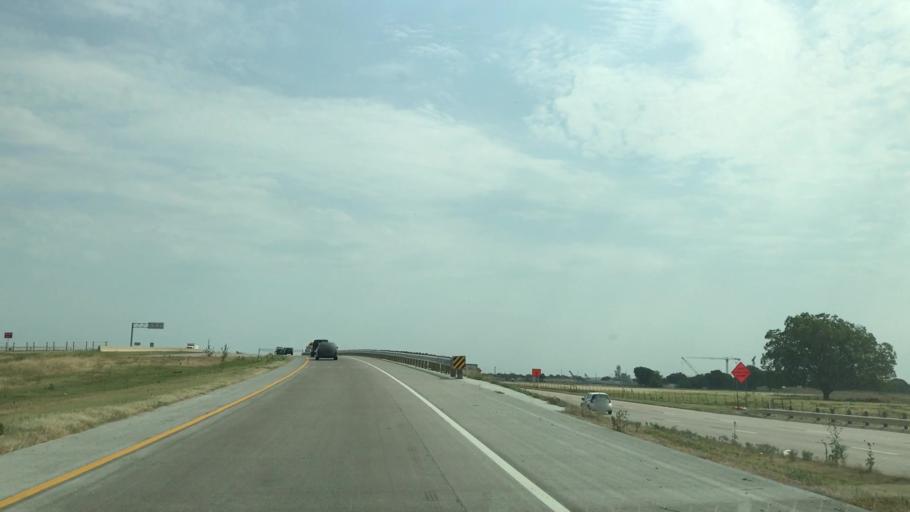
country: US
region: Texas
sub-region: Denton County
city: Roanoke
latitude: 32.9885
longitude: -97.2259
